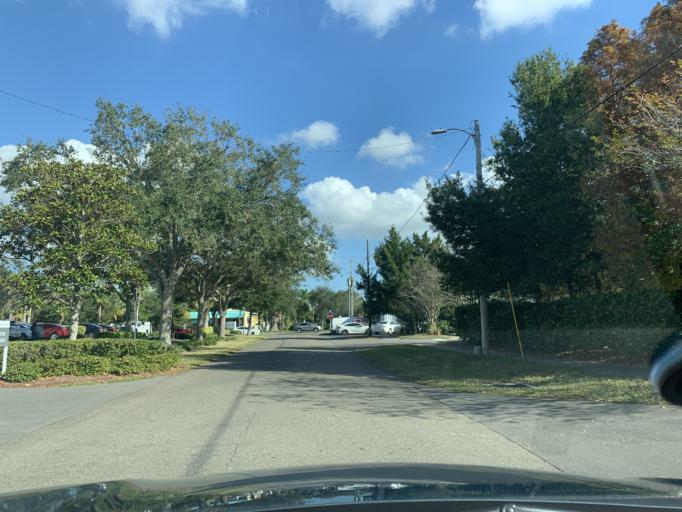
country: US
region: Florida
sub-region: Pinellas County
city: Belleair
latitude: 27.9250
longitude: -82.7973
